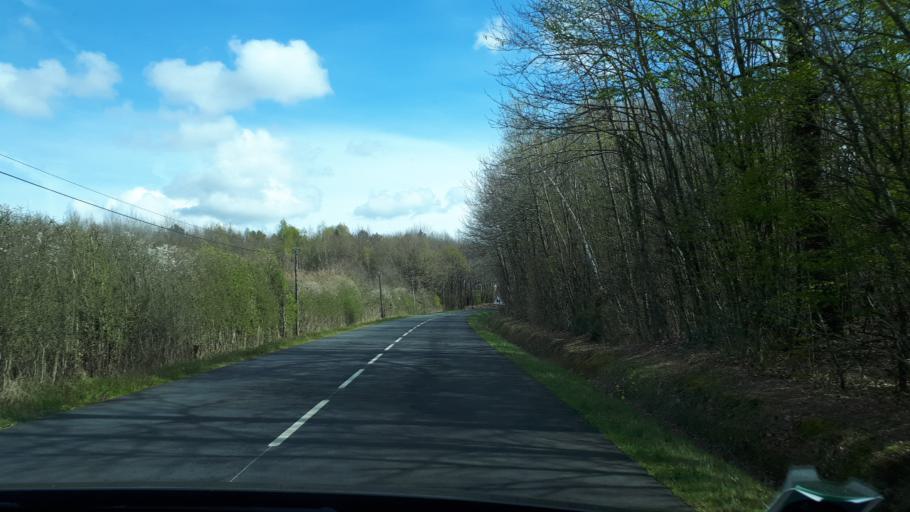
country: FR
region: Pays de la Loire
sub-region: Departement de la Sarthe
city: Le Grand-Luce
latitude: 47.8876
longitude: 0.5390
